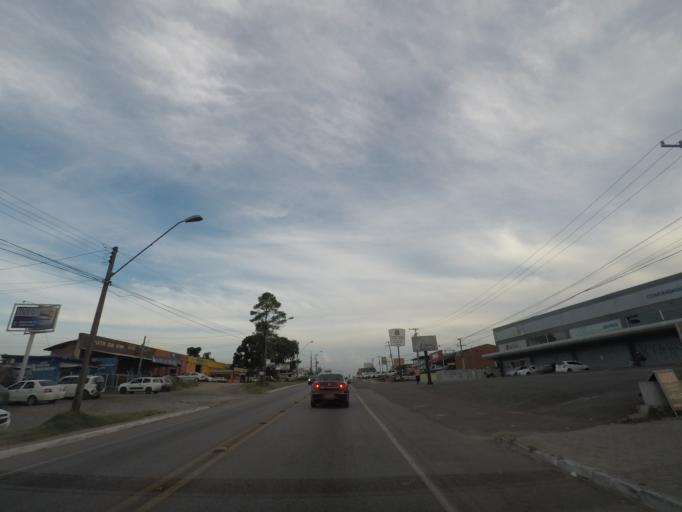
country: BR
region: Parana
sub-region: Colombo
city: Colombo
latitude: -25.3545
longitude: -49.2189
